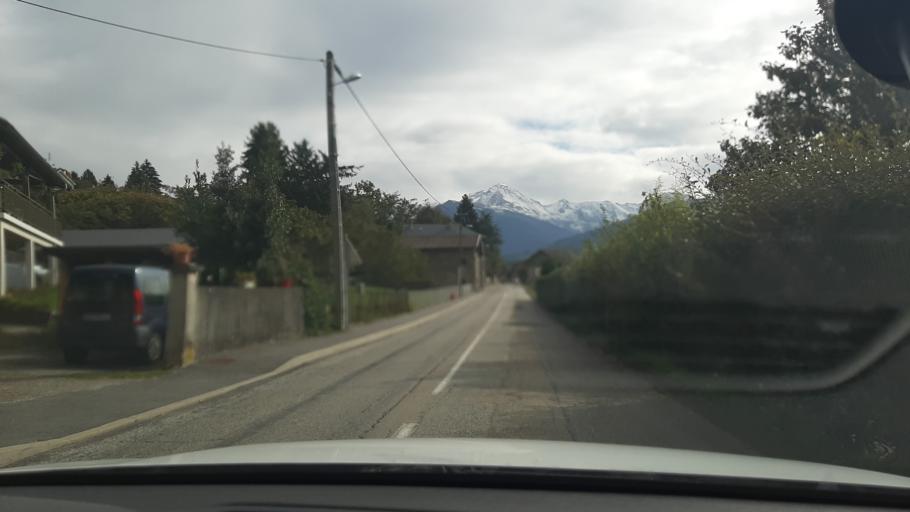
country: FR
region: Rhone-Alpes
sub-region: Departement de la Savoie
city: Montmelian
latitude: 45.4491
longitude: 6.0659
